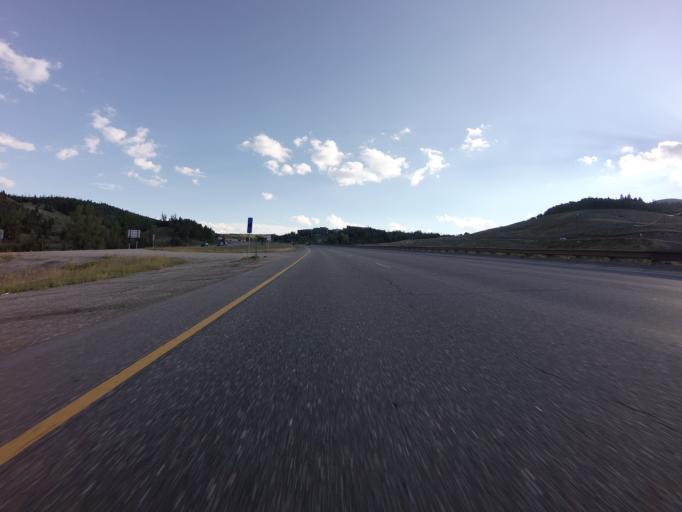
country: US
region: Colorado
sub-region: Summit County
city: Silverthorne
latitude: 39.6242
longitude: -106.0730
